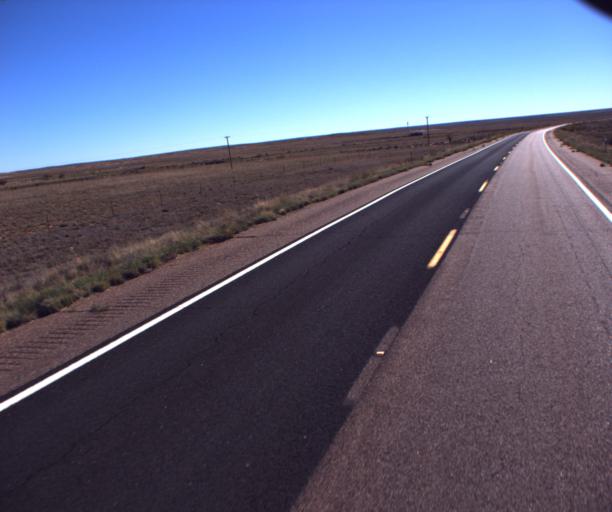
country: US
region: Arizona
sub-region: Navajo County
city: Holbrook
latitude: 34.7743
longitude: -109.8277
